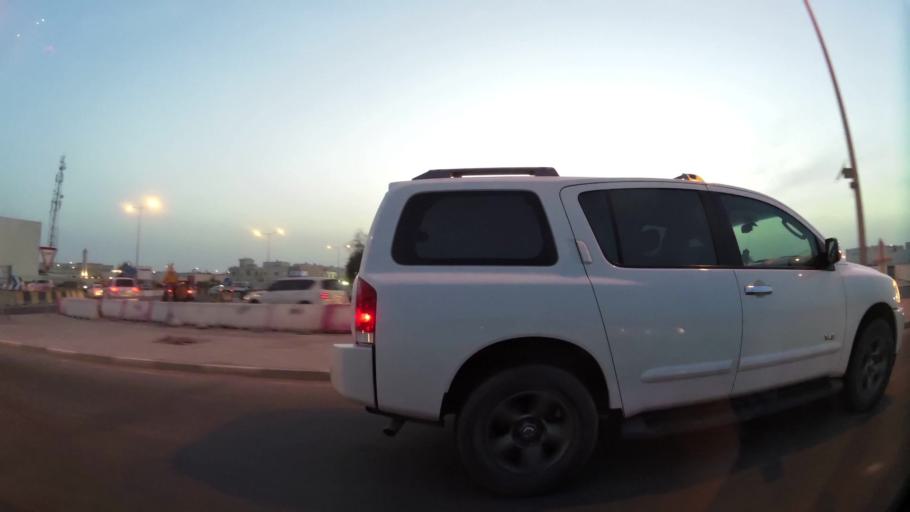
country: QA
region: Al Wakrah
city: Al Wakrah
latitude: 25.1729
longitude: 51.5975
